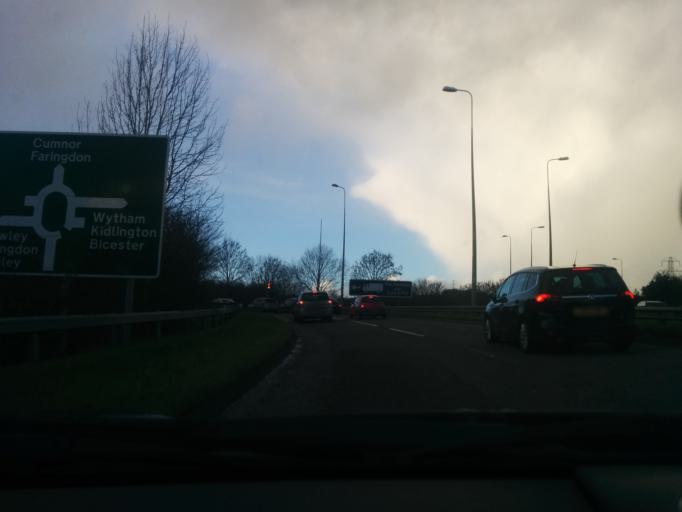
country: GB
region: England
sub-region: Oxfordshire
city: Oxford
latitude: 51.7553
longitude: -1.2938
